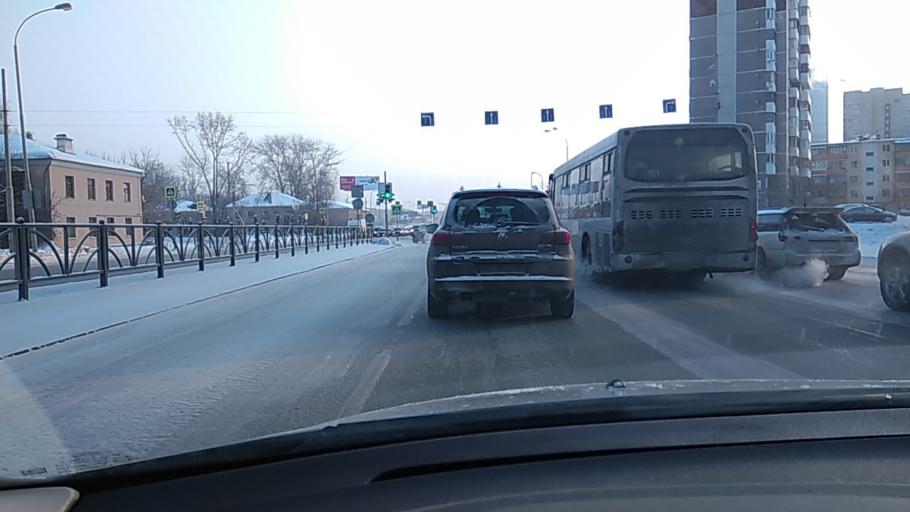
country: RU
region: Sverdlovsk
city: Yekaterinburg
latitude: 56.8025
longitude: 60.6360
